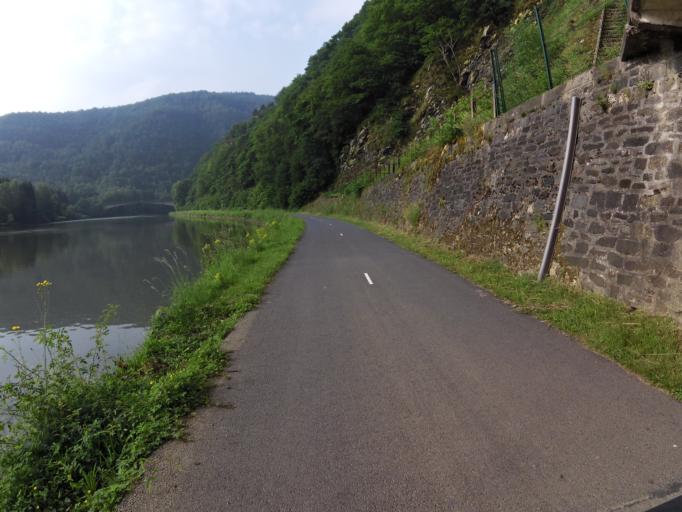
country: FR
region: Champagne-Ardenne
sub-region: Departement des Ardennes
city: Deville
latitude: 49.9095
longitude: 4.6879
